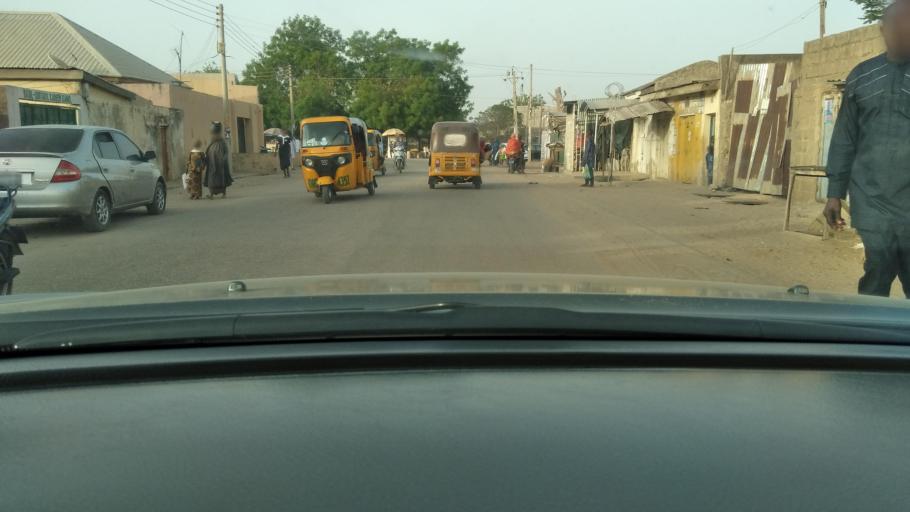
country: NG
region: Kano
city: Kano
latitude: 11.9532
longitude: 8.5232
